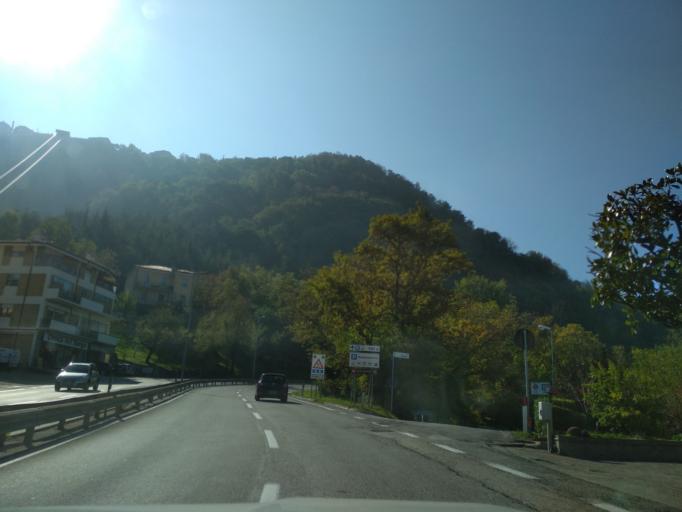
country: SM
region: Borgo Maggiore
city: Borgo Maggiore
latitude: 43.9422
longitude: 12.4444
